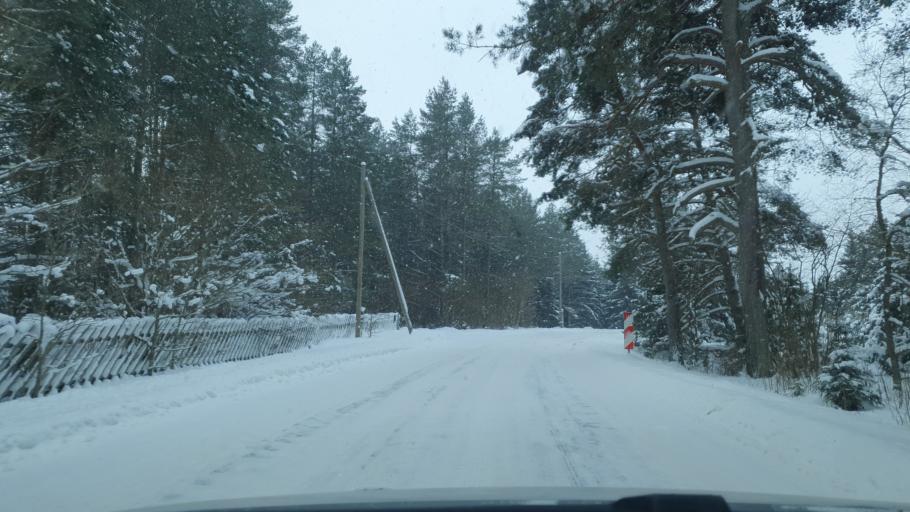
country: EE
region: Harju
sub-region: Kuusalu vald
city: Kuusalu
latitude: 59.4839
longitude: 25.3457
